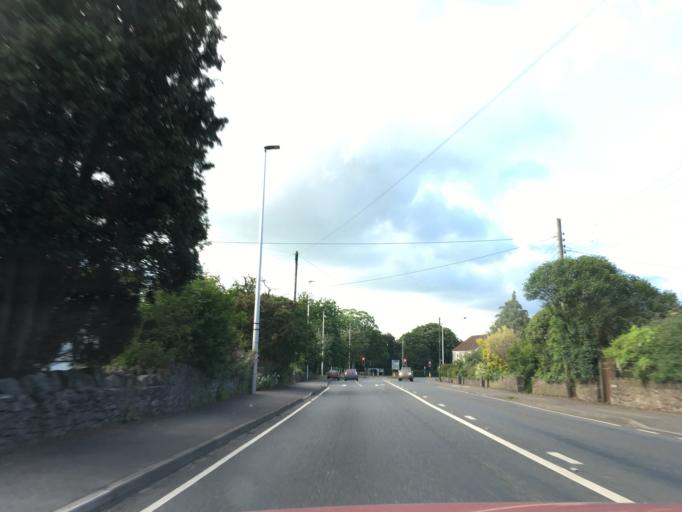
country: GB
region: England
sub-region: North Somerset
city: Churchill
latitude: 51.3333
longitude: -2.7943
